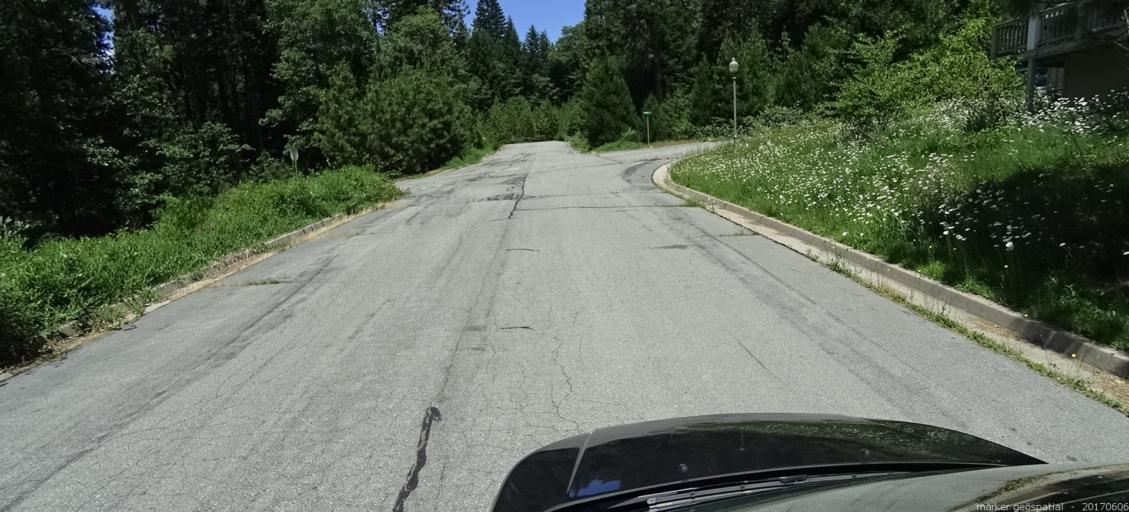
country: US
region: California
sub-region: Siskiyou County
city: Dunsmuir
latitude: 41.2301
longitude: -122.2708
